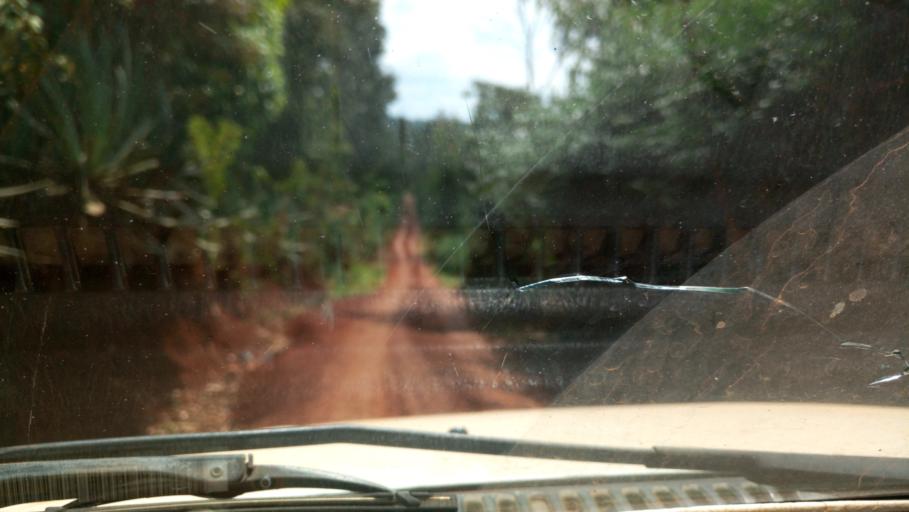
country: KE
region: Murang'a District
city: Maragua
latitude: -0.8536
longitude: 37.0900
